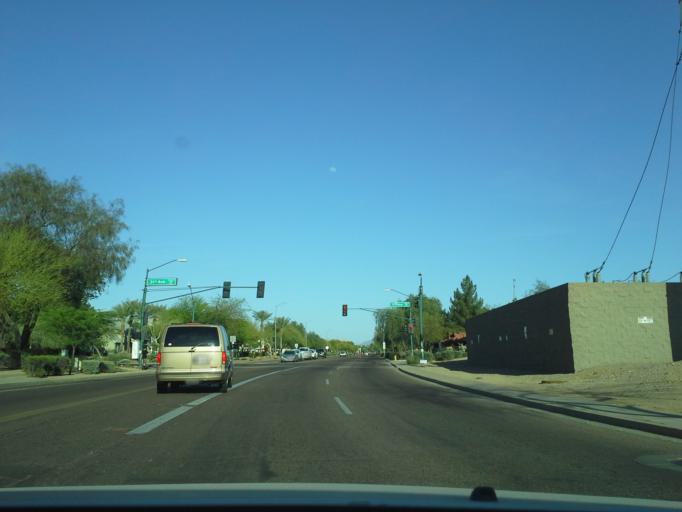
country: US
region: Arizona
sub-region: Maricopa County
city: Glendale
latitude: 33.6627
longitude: -112.1267
